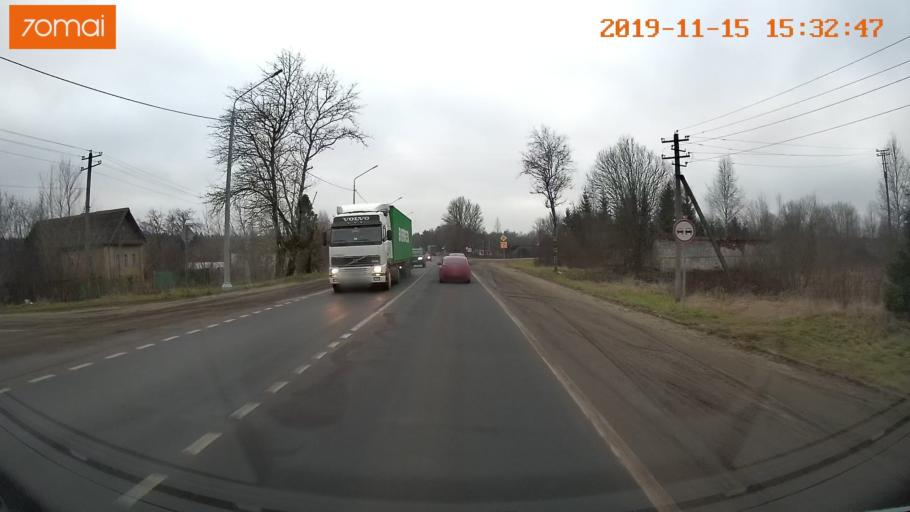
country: RU
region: Jaroslavl
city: Danilov
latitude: 58.0870
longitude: 40.0964
